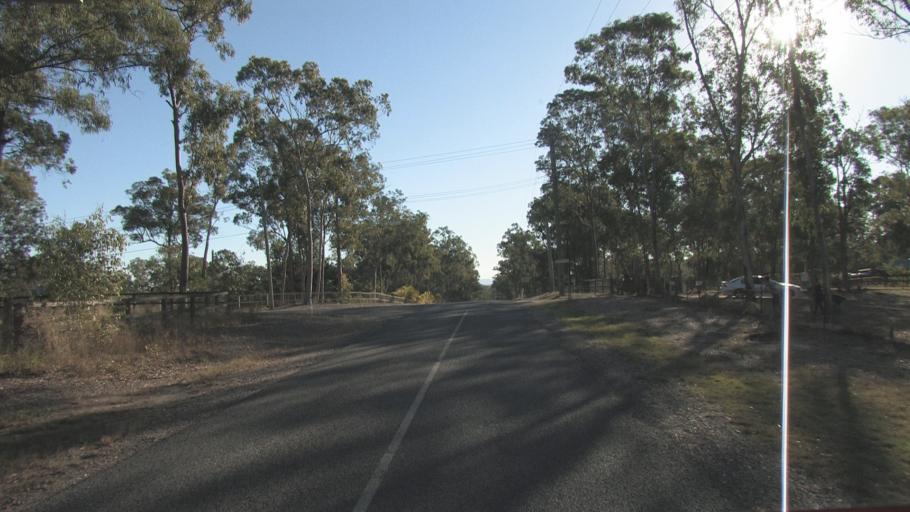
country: AU
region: Queensland
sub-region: Logan
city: Windaroo
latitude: -27.7712
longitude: 153.1426
